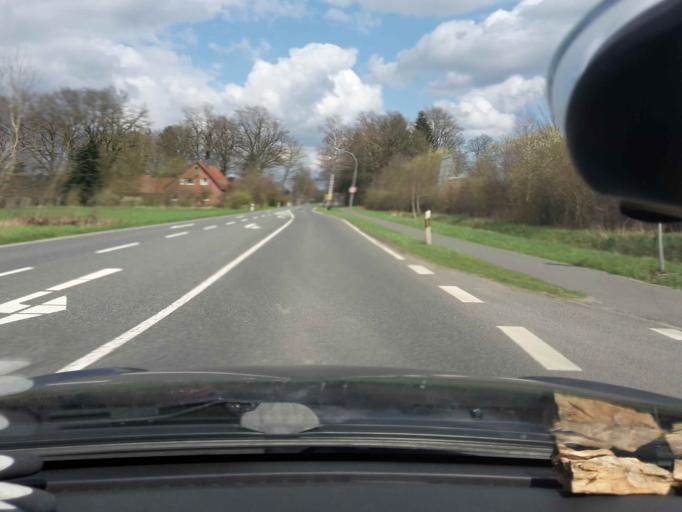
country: DE
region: Lower Saxony
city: Schneverdingen
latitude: 53.0832
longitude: 9.8668
